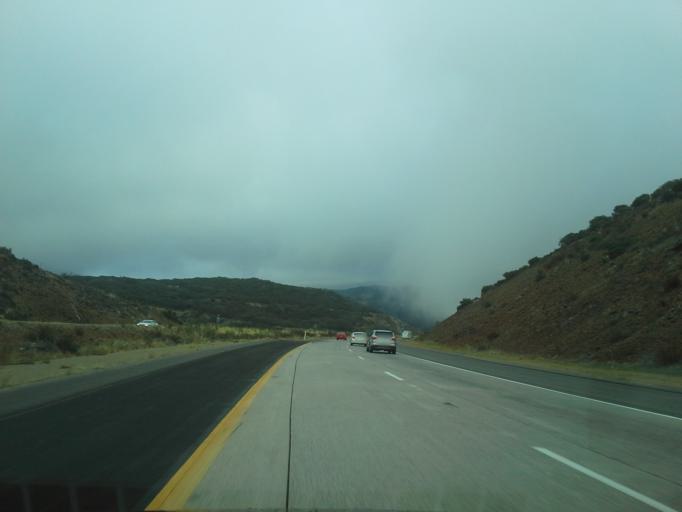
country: US
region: California
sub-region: San Diego County
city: Pine Valley
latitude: 32.8219
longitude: -116.5682
